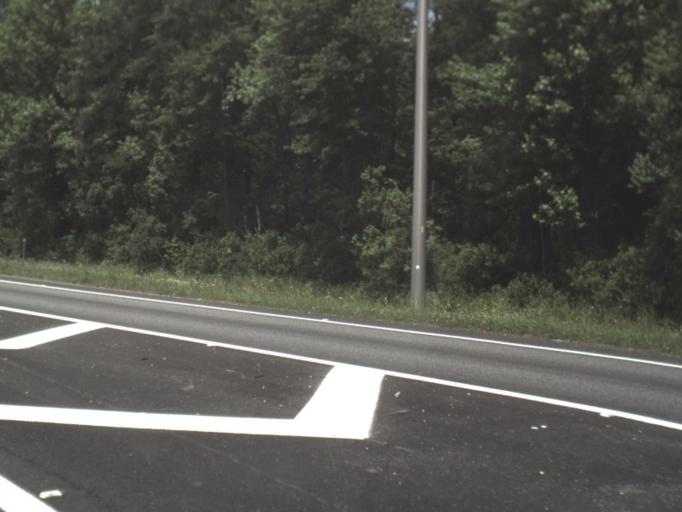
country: US
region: Florida
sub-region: Duval County
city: Jacksonville
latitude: 30.3752
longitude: -81.7609
